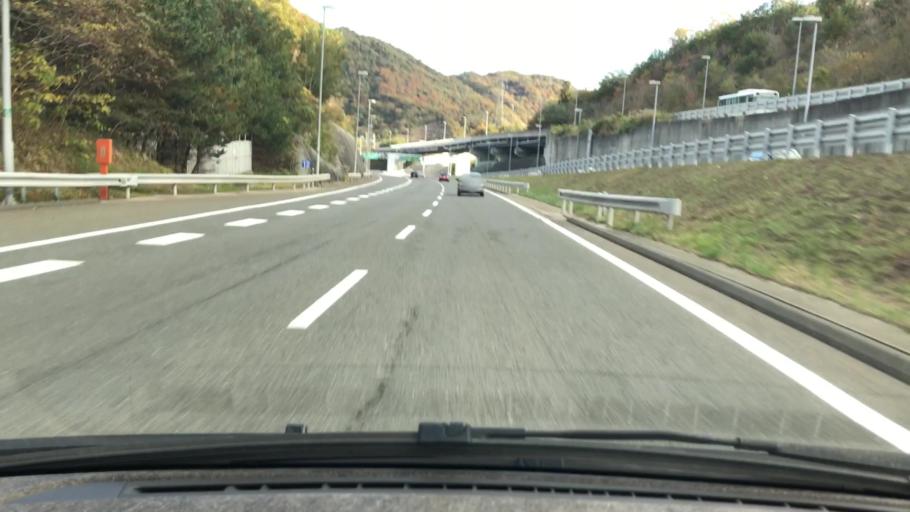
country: JP
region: Hyogo
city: Sandacho
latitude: 34.7920
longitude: 135.2251
